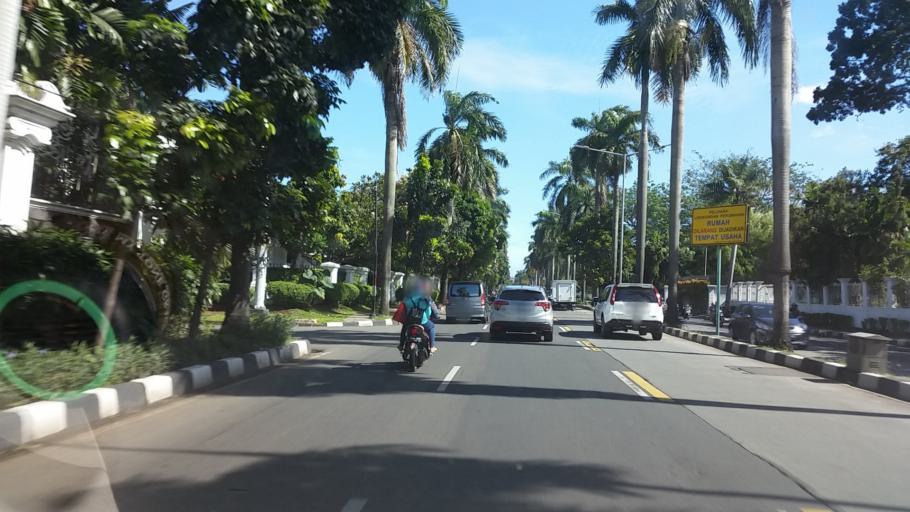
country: ID
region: Banten
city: South Tangerang
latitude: -6.2781
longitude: 106.7814
